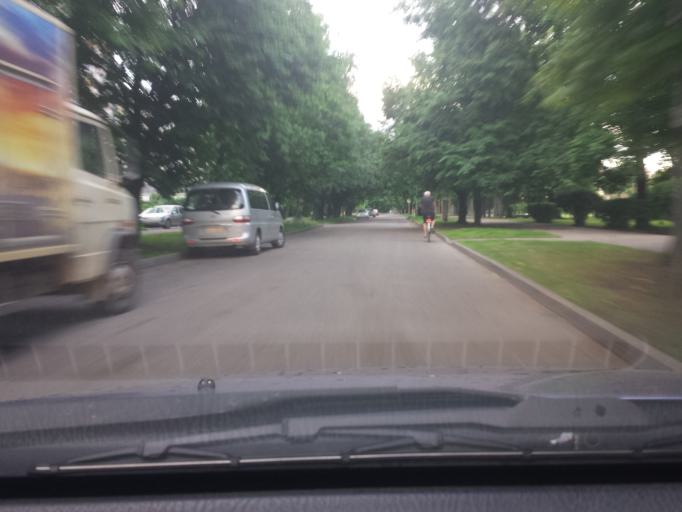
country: LV
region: Riga
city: Jaunciems
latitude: 56.9681
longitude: 24.1823
